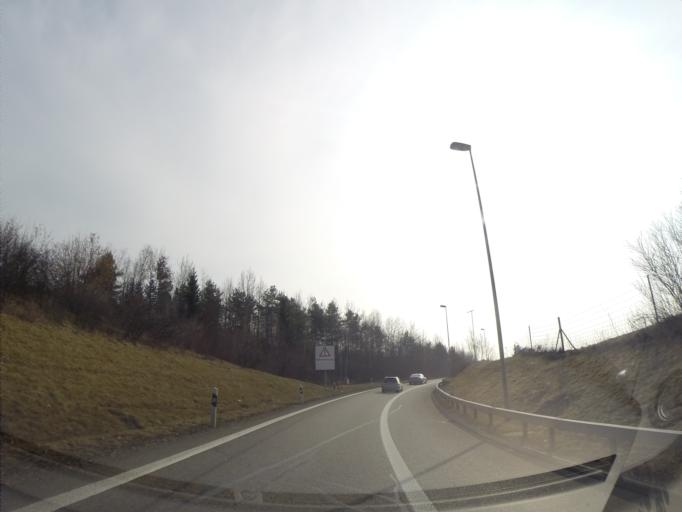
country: CH
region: Zurich
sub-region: Bezirk Winterthur
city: Wuelflingen (Kreis 6) / Lindenplatz
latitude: 47.5248
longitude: 8.7011
